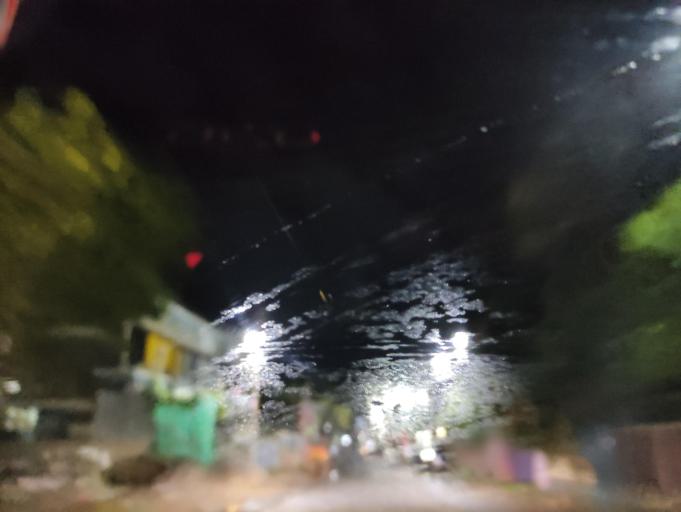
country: IN
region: Kerala
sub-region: Thiruvananthapuram
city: Thiruvananthapuram
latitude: 8.4657
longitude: 76.9279
